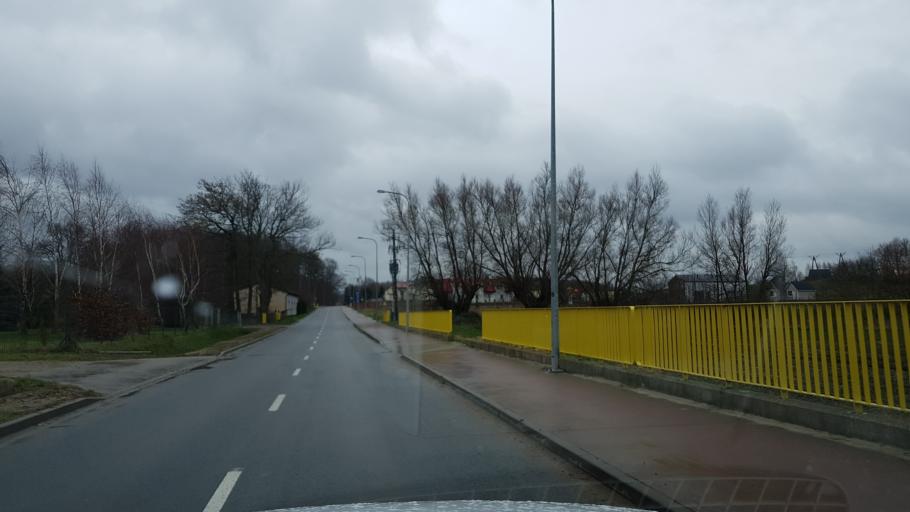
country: PL
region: West Pomeranian Voivodeship
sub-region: Powiat kolobrzeski
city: Ustronie Morskie
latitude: 54.2094
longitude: 15.7659
